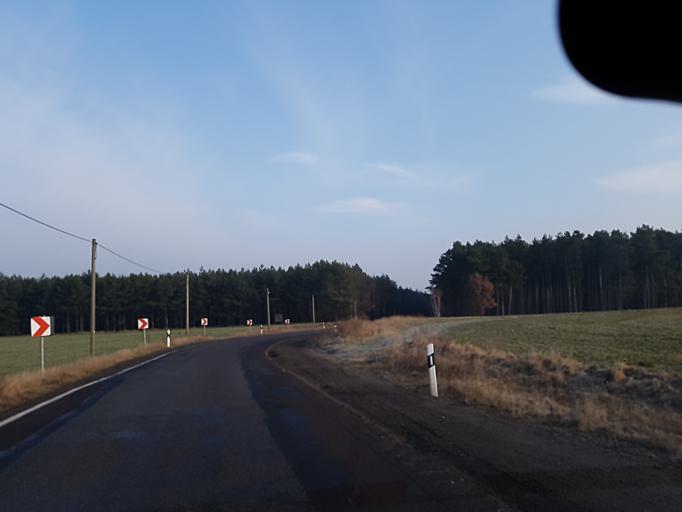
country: DE
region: Brandenburg
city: Gorzke
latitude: 52.1926
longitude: 12.3843
